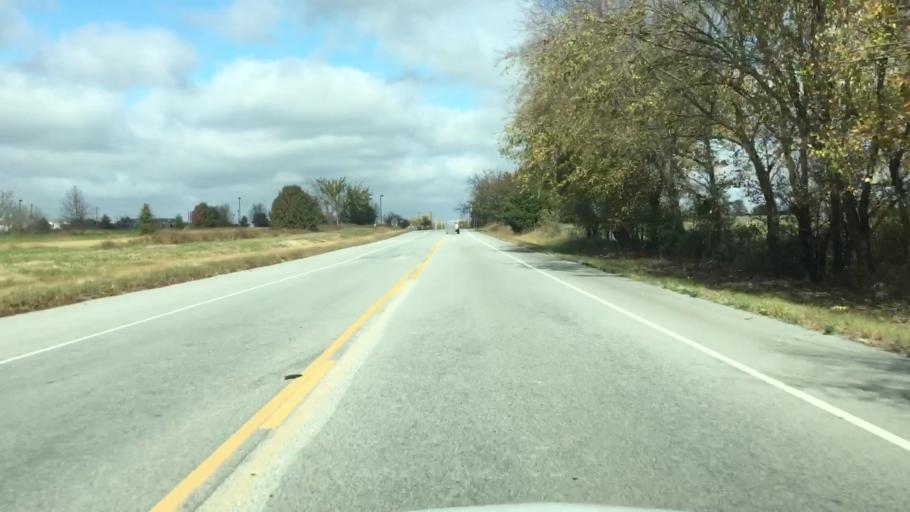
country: US
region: Arkansas
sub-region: Benton County
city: Centerton
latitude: 36.3058
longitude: -94.3039
